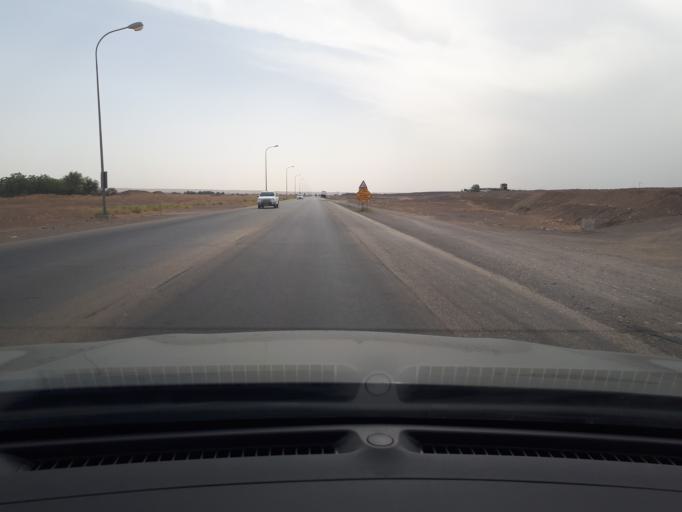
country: OM
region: Ash Sharqiyah
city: Badiyah
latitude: 22.4652
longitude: 58.8718
